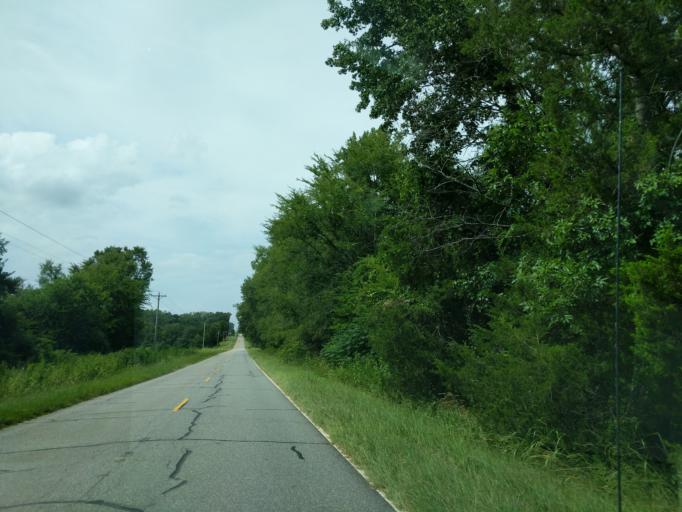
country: US
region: South Carolina
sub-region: Abbeville County
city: Calhoun Falls
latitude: 34.1722
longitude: -82.6047
